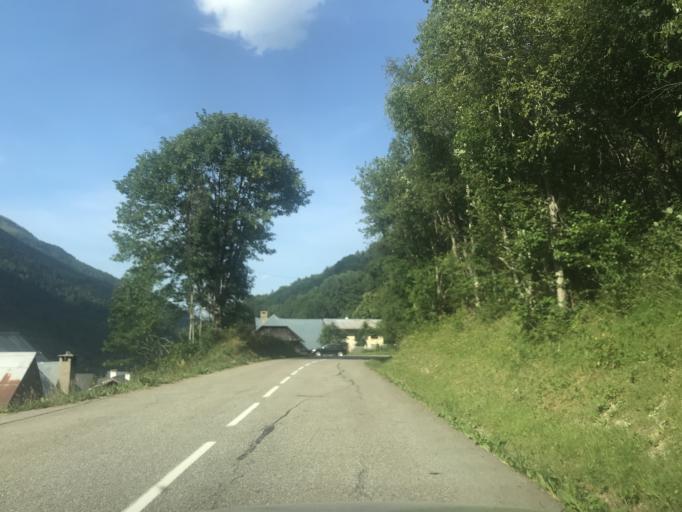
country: FR
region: Rhone-Alpes
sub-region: Departement de la Savoie
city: Saint-Etienne-de-Cuines
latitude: 45.2804
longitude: 6.2118
